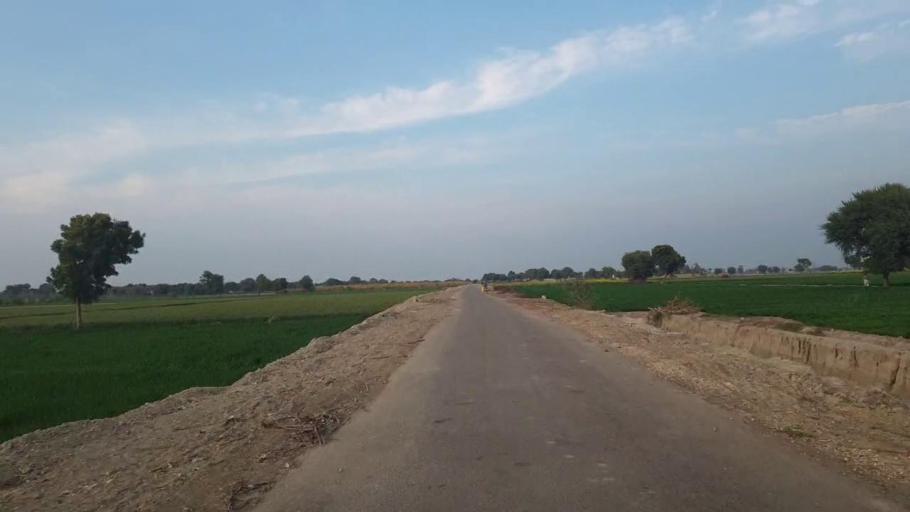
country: PK
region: Sindh
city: Shahpur Chakar
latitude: 26.1045
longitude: 68.5465
